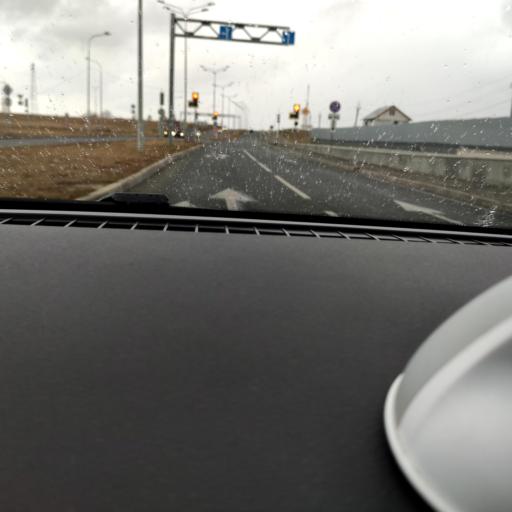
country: RU
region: Samara
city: Samara
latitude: 53.2815
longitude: 50.2427
